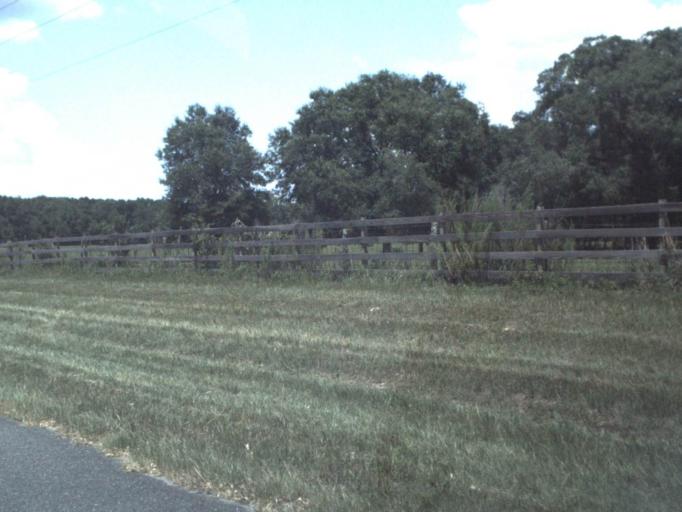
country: US
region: Florida
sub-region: Dixie County
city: Cross City
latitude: 29.6992
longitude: -82.9843
